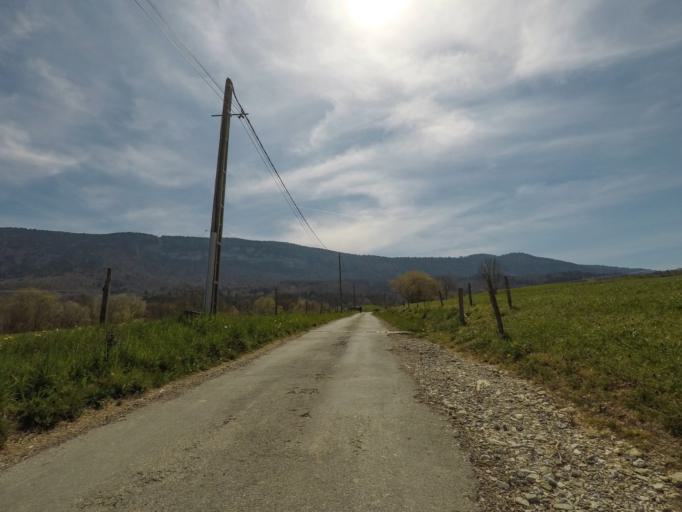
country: FR
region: Rhone-Alpes
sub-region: Departement de la Haute-Savoie
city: Archamps
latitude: 46.1225
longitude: 6.1370
